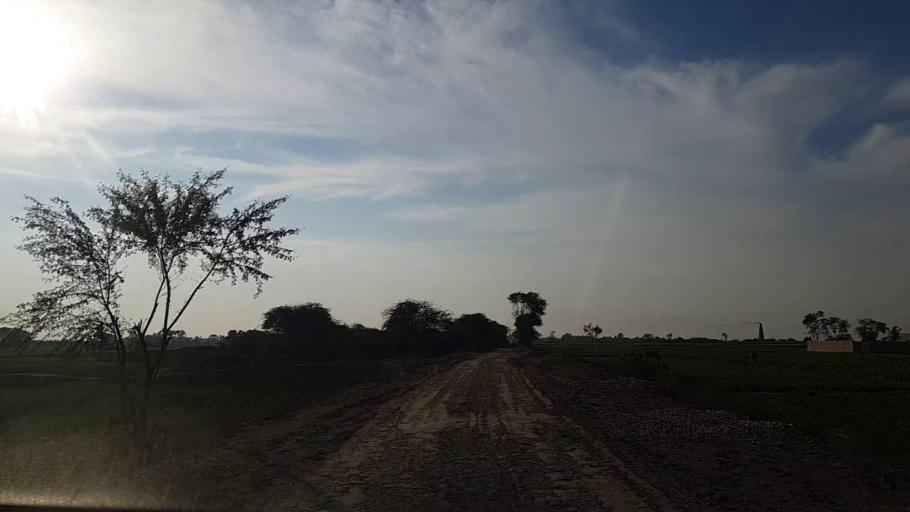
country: PK
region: Sindh
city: Bandhi
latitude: 26.5535
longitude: 68.2459
